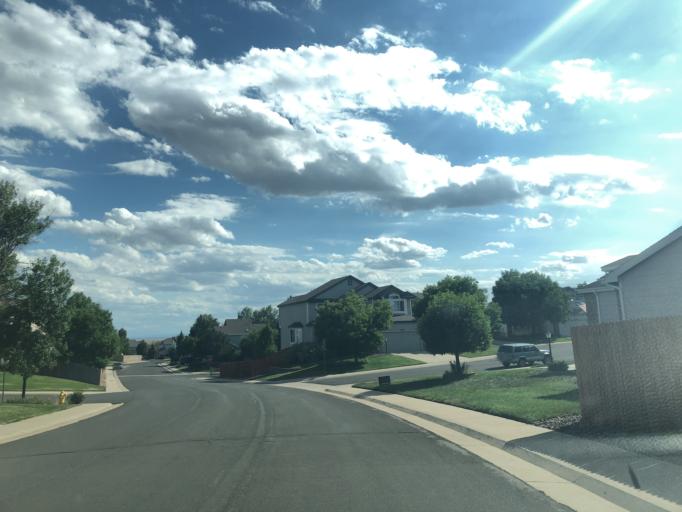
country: US
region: Colorado
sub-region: Arapahoe County
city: Dove Valley
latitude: 39.6162
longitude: -104.7715
